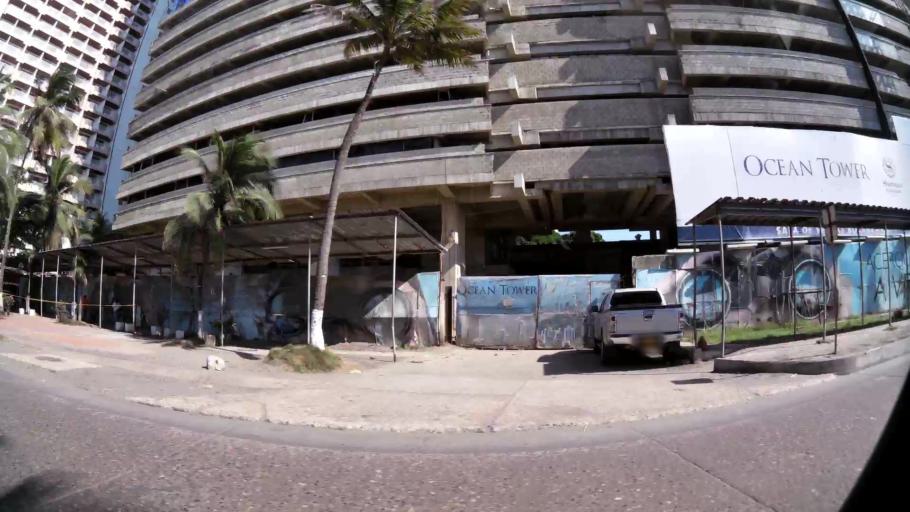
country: CO
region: Bolivar
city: Cartagena
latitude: 10.4037
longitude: -75.5559
